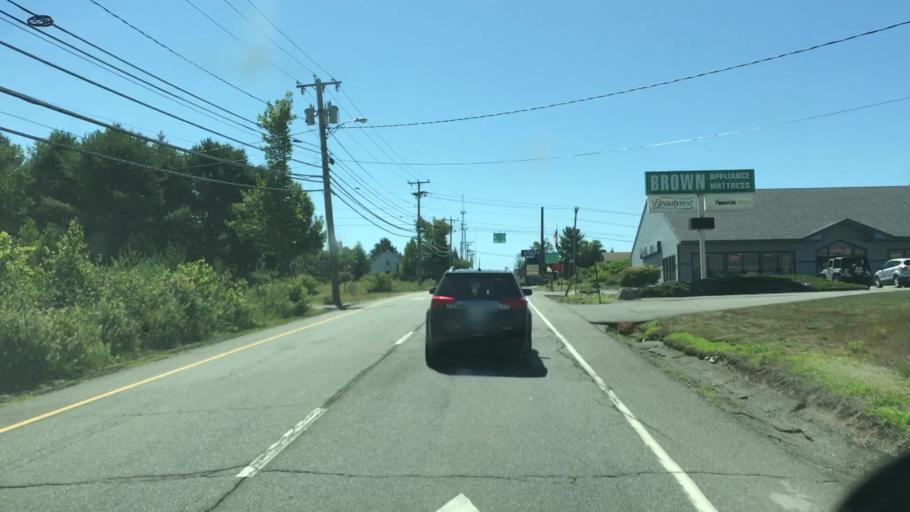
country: US
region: Maine
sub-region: Hancock County
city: Ellsworth
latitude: 44.5270
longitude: -68.4016
